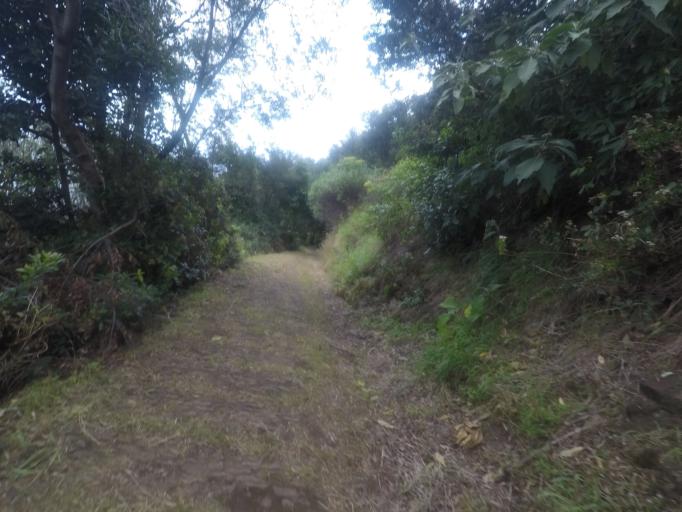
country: PT
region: Madeira
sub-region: Santana
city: Santana
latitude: 32.8274
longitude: -16.8954
